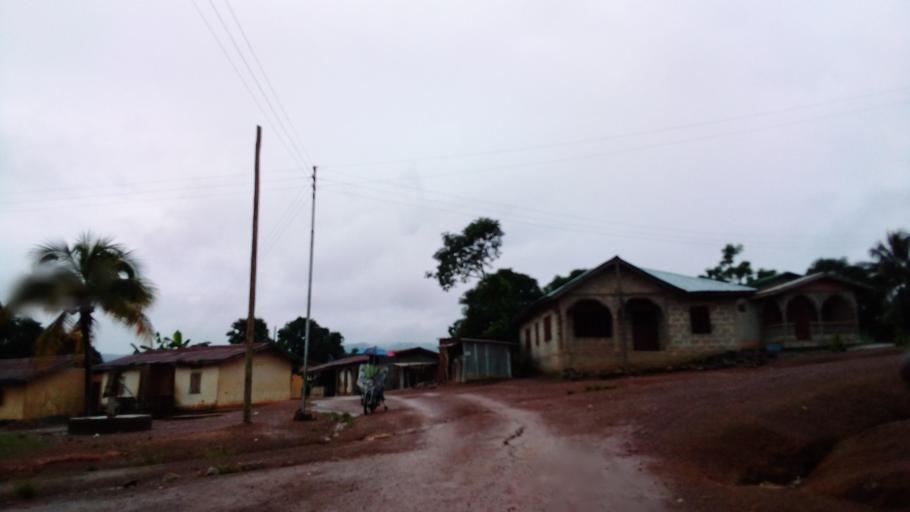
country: SL
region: Eastern Province
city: Kenema
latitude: 7.8686
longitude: -11.1749
